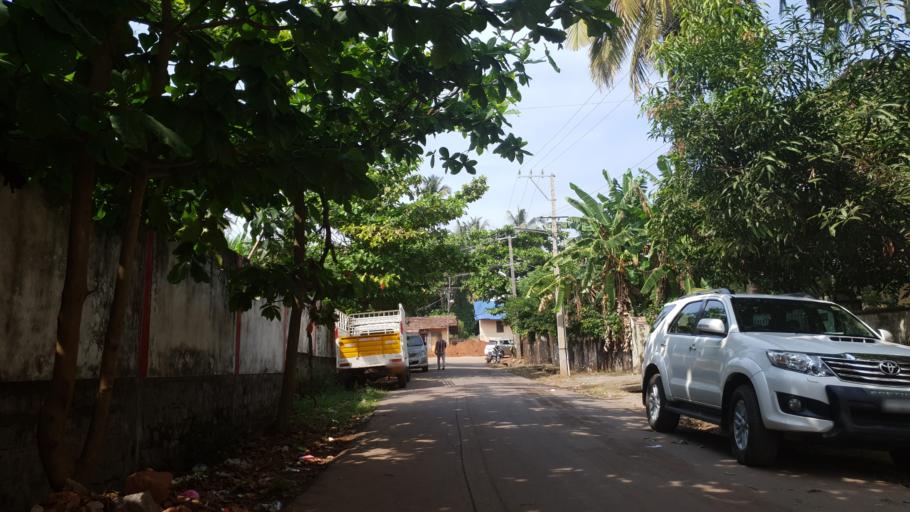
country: IN
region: Karnataka
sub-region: Dakshina Kannada
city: Ullal
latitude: 12.8462
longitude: 74.8435
